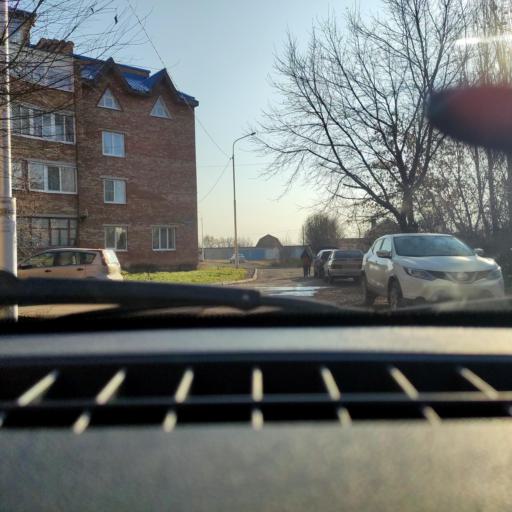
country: RU
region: Bashkortostan
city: Ufa
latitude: 54.5706
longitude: 55.9040
